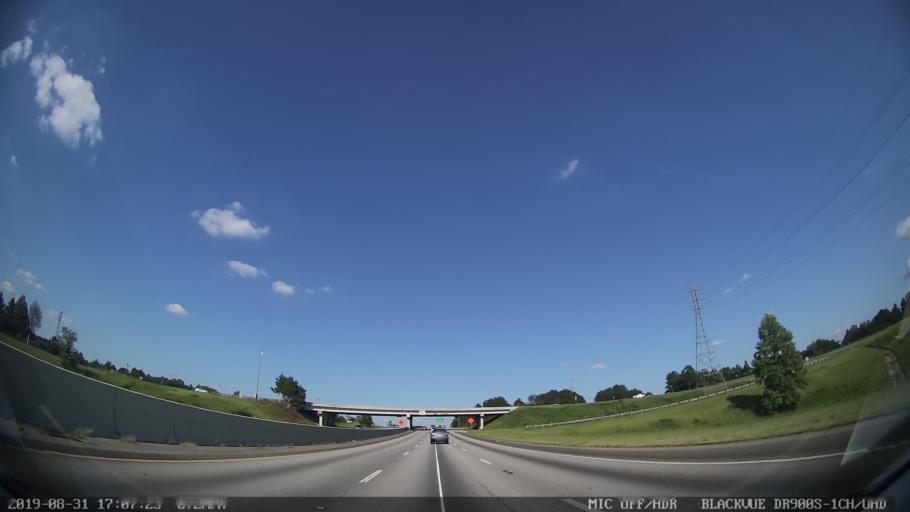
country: US
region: South Carolina
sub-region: Spartanburg County
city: Fairforest
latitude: 34.9610
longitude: -82.0552
